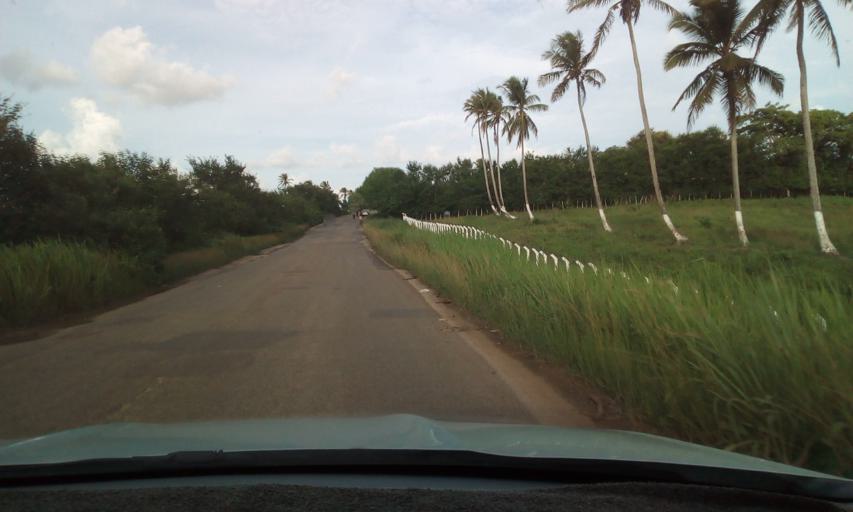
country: BR
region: Pernambuco
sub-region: Gloria Do Goita
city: Gloria do Goita
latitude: -7.9888
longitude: -35.2432
